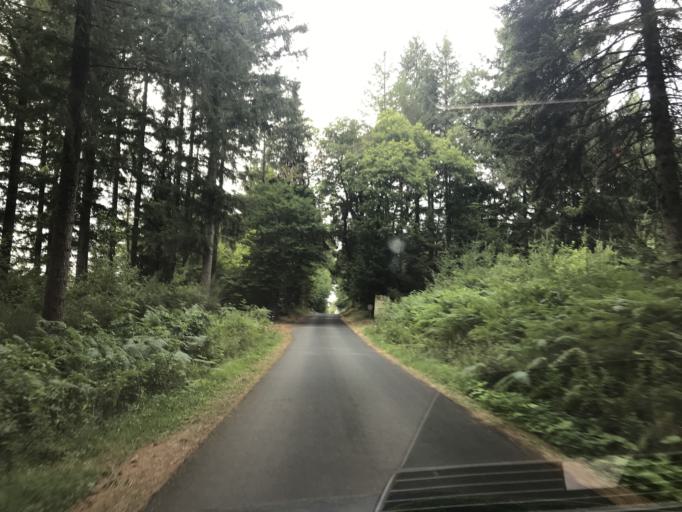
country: FR
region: Limousin
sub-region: Departement de la Correze
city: Neuvic
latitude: 45.3806
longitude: 2.2306
